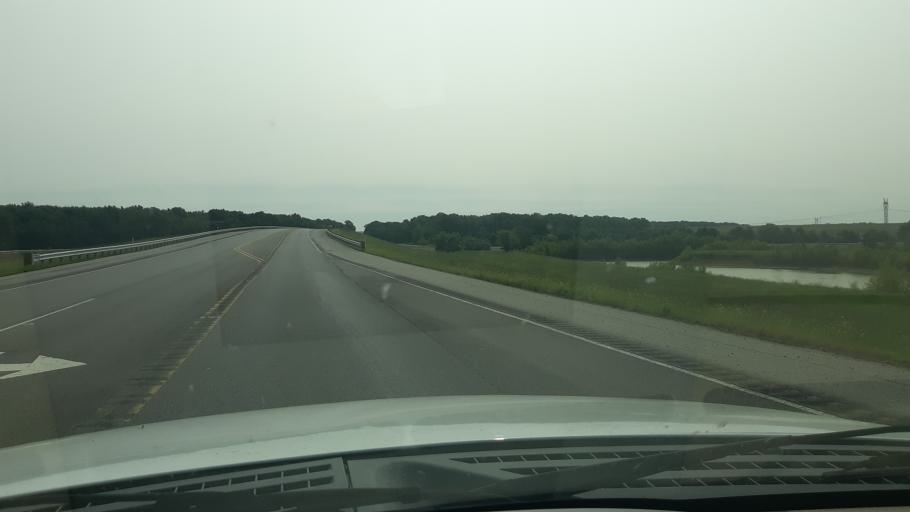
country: US
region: Illinois
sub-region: Wabash County
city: Mount Carmel
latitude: 38.3916
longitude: -87.7433
